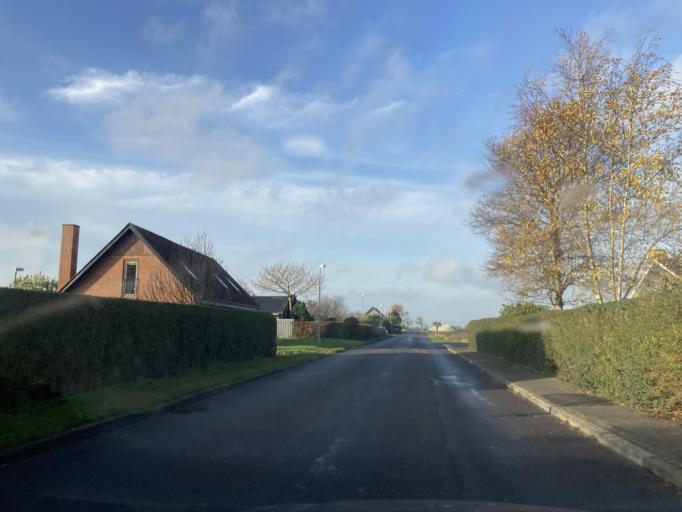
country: DK
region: Zealand
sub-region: Lolland Kommune
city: Rodby
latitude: 54.6887
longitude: 11.3816
